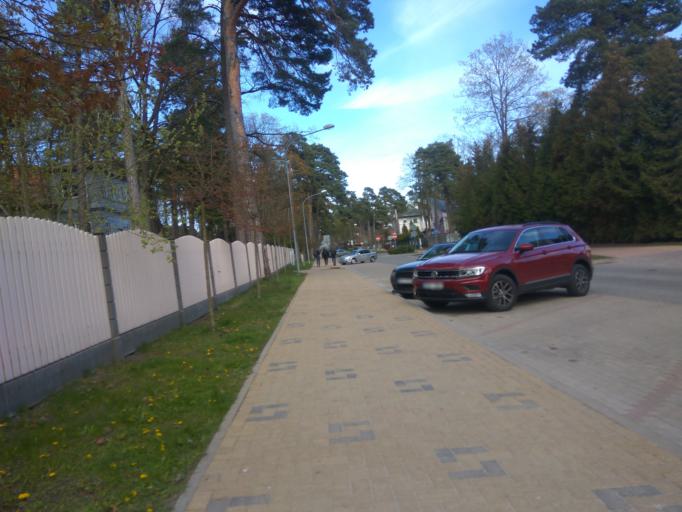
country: LV
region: Jurmala
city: Jurmala
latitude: 56.9761
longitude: 23.8043
